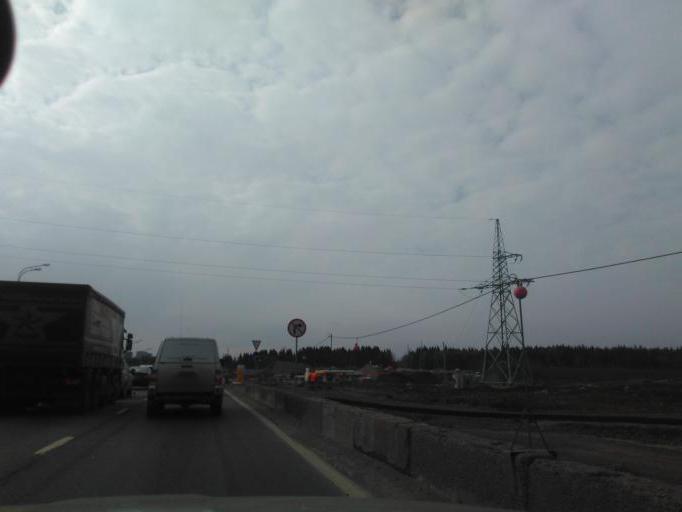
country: RU
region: Moskovskaya
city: Yermolino
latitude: 56.1437
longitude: 37.4922
